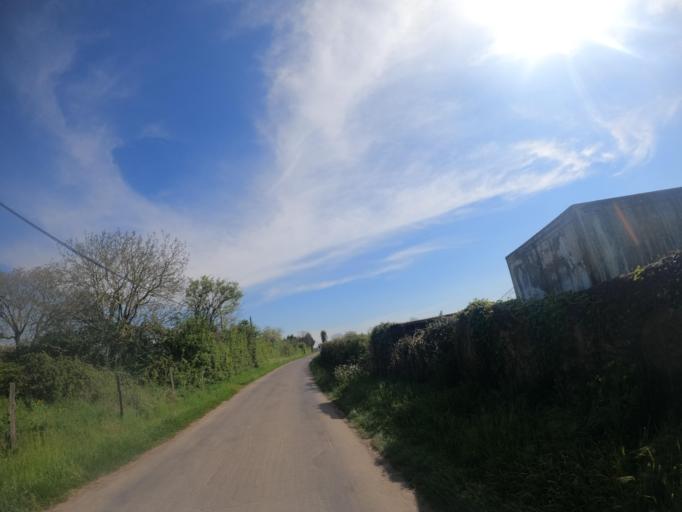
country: FR
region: Poitou-Charentes
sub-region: Departement des Deux-Sevres
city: Saint-Varent
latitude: 46.9145
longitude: -0.2170
